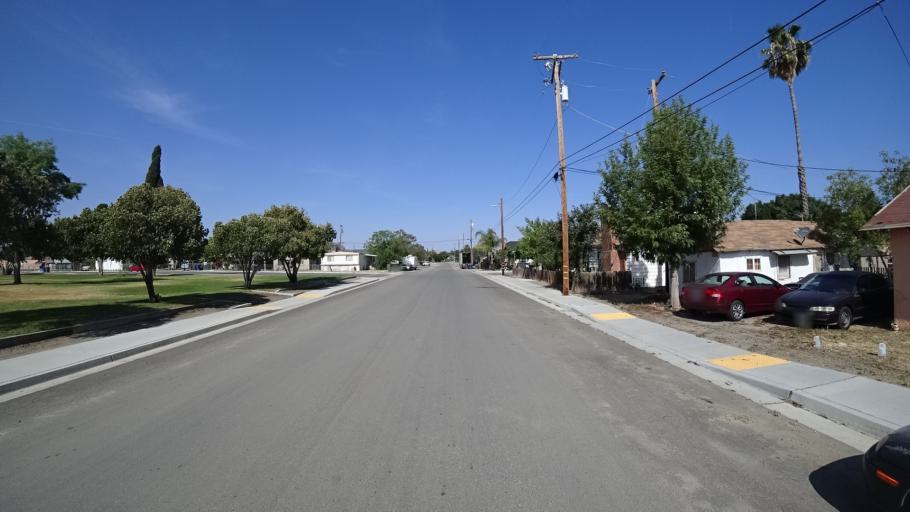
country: US
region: California
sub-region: Kings County
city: Kettleman City
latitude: 36.0094
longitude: -119.9621
